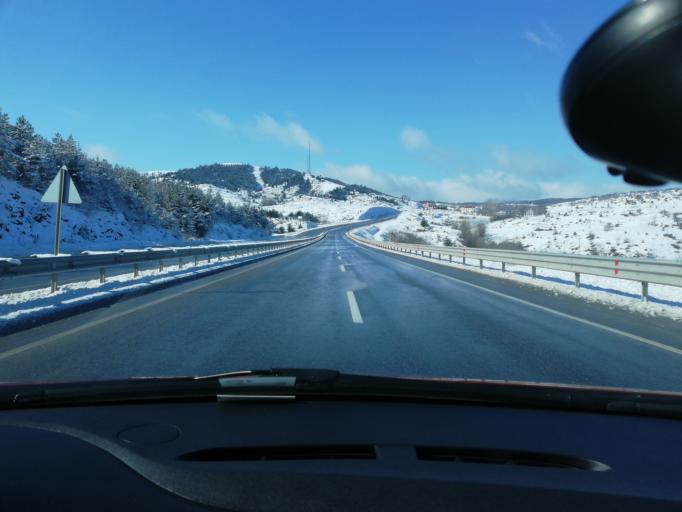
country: TR
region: Kastamonu
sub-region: Cide
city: Kastamonu
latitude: 41.3593
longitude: 33.6777
